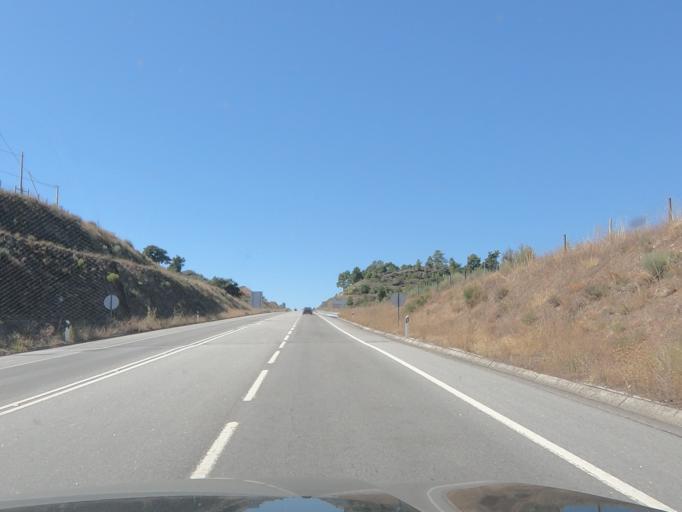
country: PT
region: Vila Real
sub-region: Valpacos
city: Valpacos
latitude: 41.5670
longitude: -7.2746
